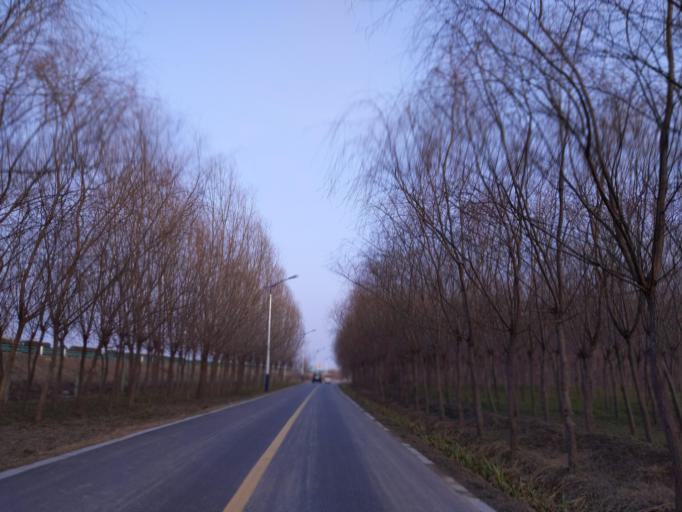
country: CN
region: Henan Sheng
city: Puyang
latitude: 35.8211
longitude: 115.0177
